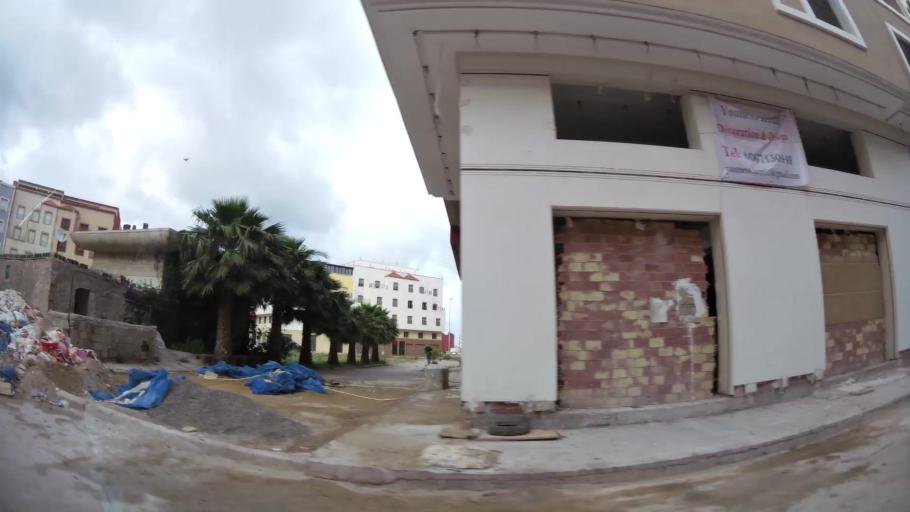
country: MA
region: Oriental
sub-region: Nador
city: Nador
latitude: 35.1546
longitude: -2.9277
